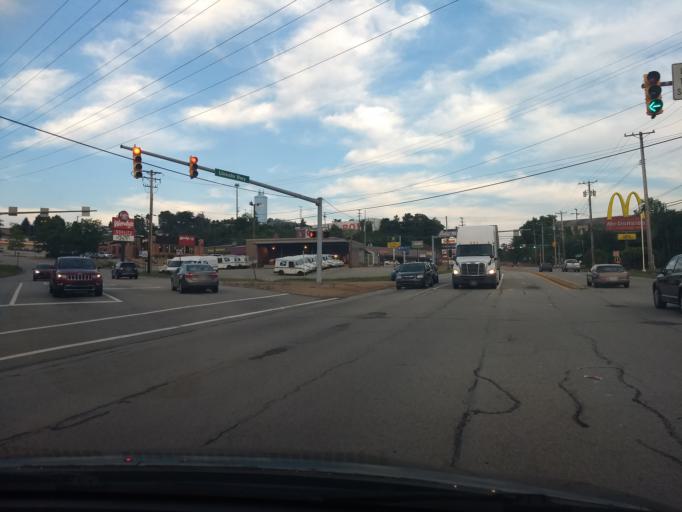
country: US
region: Pennsylvania
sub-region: Allegheny County
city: Wilmerding
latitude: 40.3847
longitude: -79.8243
